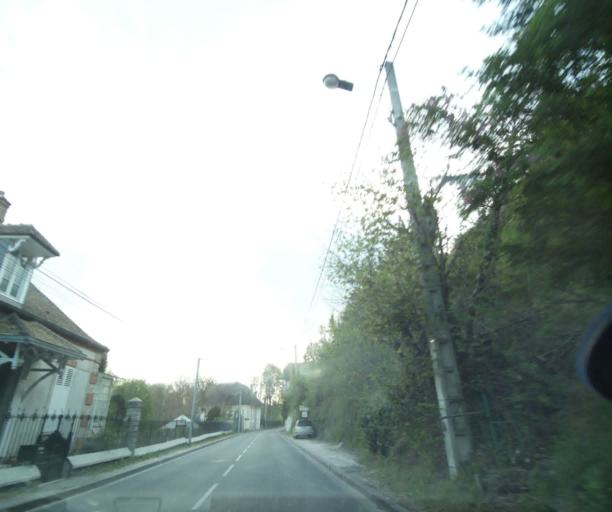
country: FR
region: Ile-de-France
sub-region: Departement de Seine-et-Marne
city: Montigny-sur-Loing
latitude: 48.3360
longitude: 2.7582
